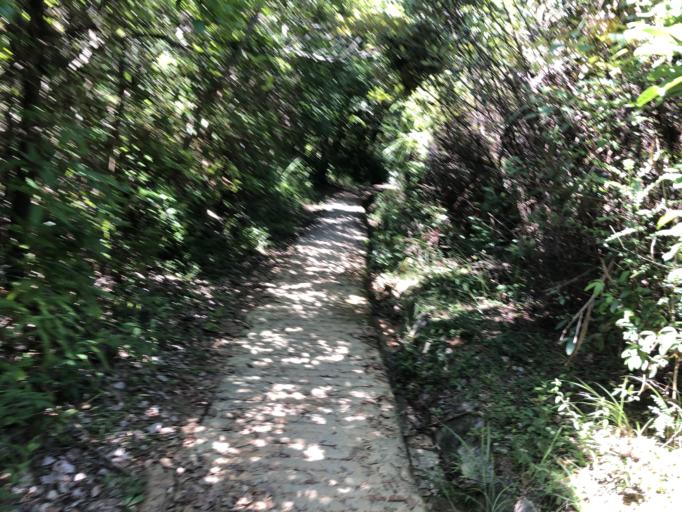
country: HK
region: Tuen Mun
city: Tuen Mun
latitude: 22.2816
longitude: 113.9836
